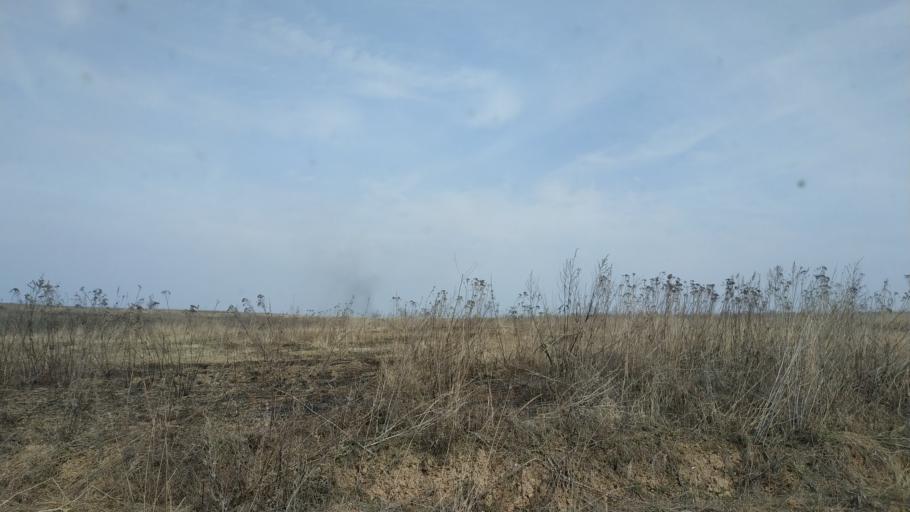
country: RU
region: Moskovskaya
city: Troitskoye
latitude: 55.3587
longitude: 38.4617
